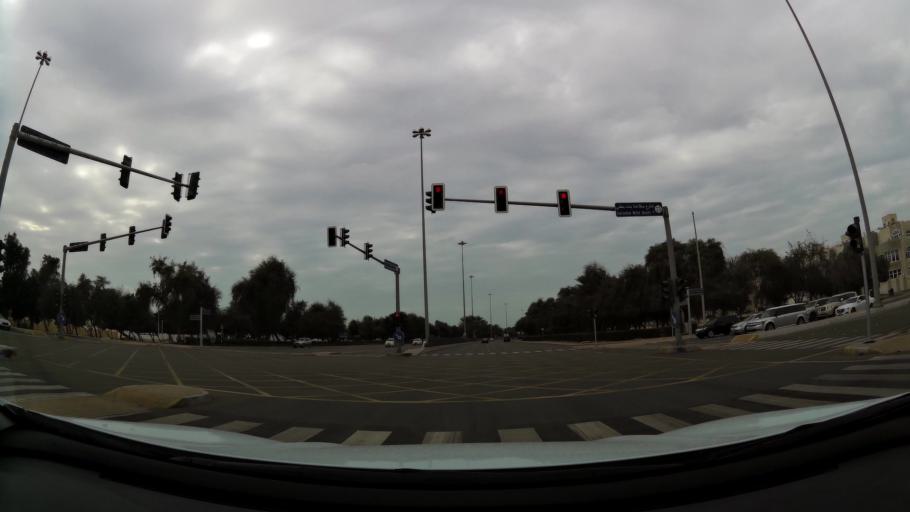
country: AE
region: Abu Dhabi
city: Abu Dhabi
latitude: 24.4364
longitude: 54.4048
